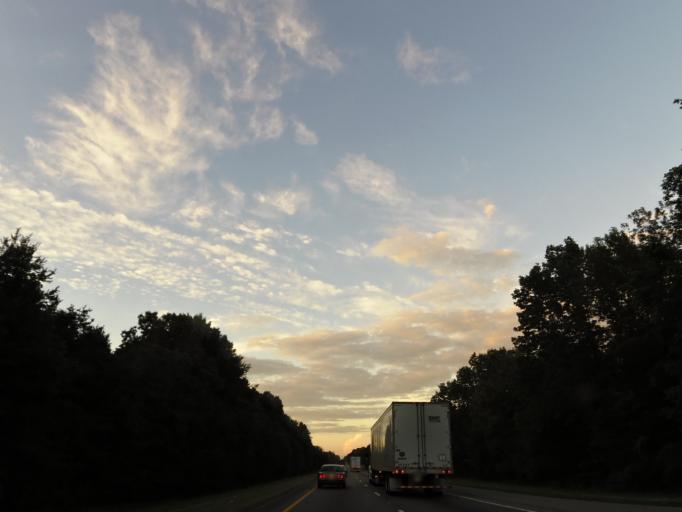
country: US
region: Tennessee
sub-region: Monroe County
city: Sweetwater
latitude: 35.5576
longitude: -84.5557
